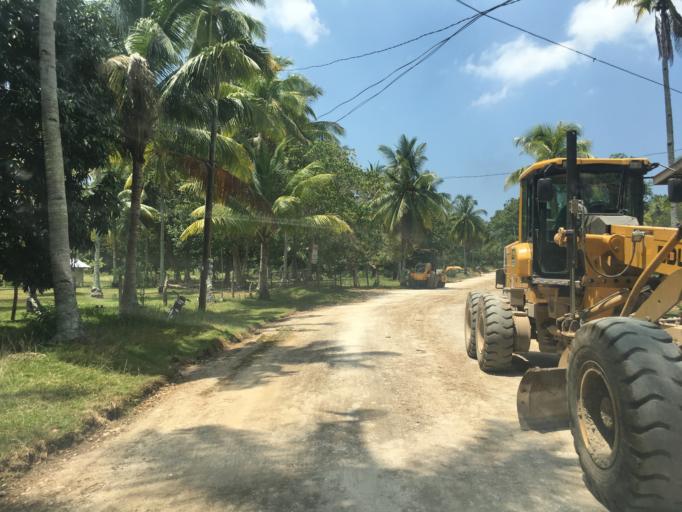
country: PH
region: Davao
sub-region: Province of Davao del Norte
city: Kaputian
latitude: 6.9337
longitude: 125.7143
